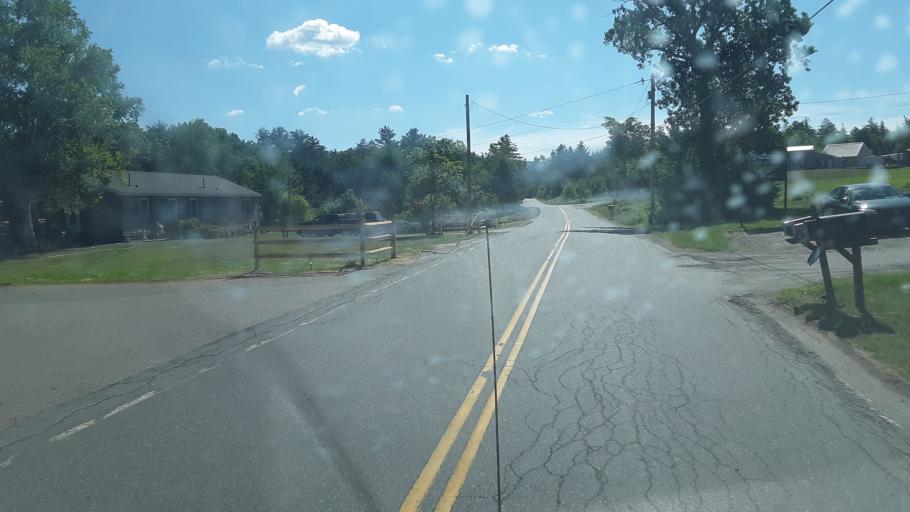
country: US
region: New Hampshire
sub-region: Grafton County
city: North Haverhill
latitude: 44.0979
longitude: -71.8783
